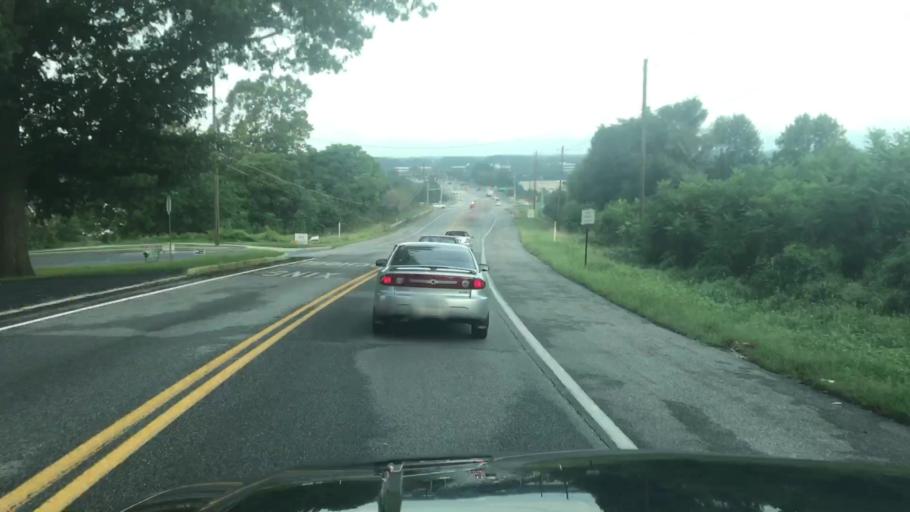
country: US
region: Pennsylvania
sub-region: Cumberland County
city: Shiremanstown
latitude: 40.2027
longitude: -76.9533
